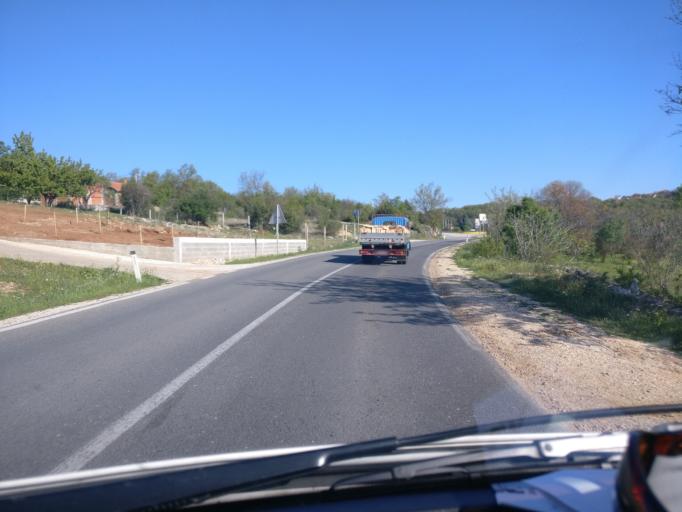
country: BA
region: Federation of Bosnia and Herzegovina
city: Crnici
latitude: 43.1069
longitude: 17.9052
